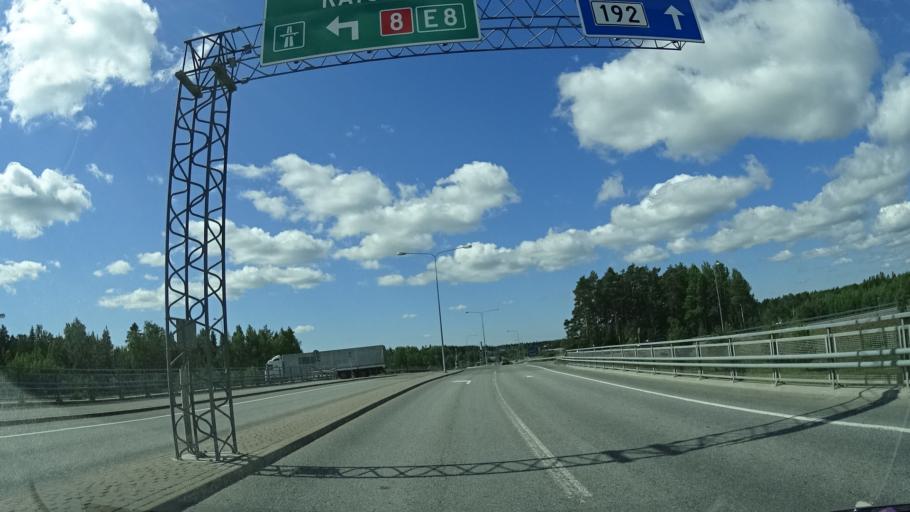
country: FI
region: Varsinais-Suomi
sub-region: Turku
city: Raisio
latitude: 60.5061
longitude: 22.1567
